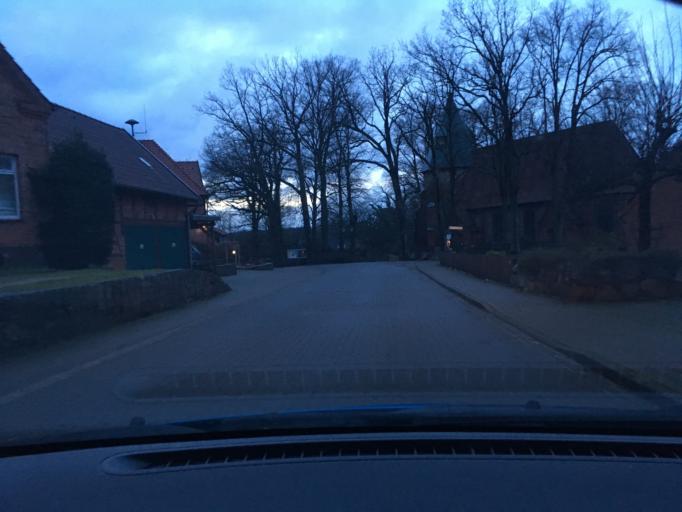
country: DE
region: Lower Saxony
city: Betzendorf
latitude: 53.1372
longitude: 10.3137
